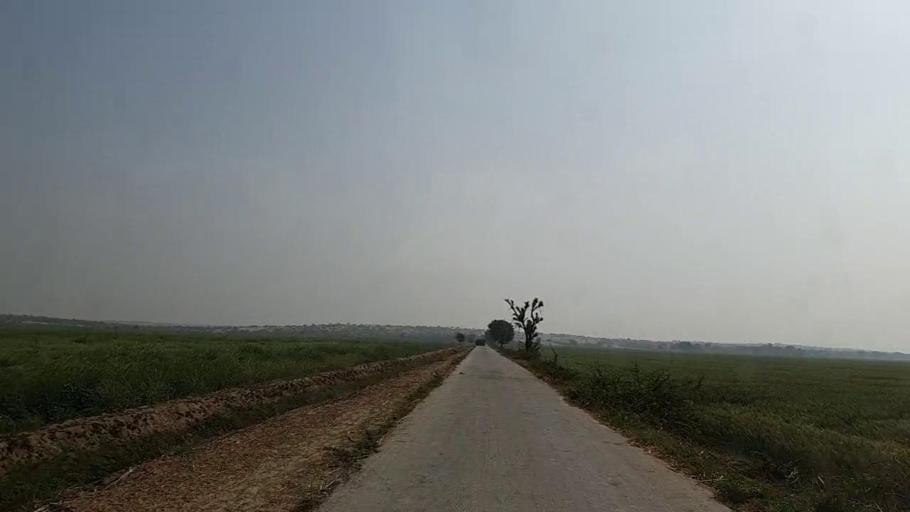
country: PK
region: Sindh
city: Naukot
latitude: 24.7545
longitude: 69.3472
